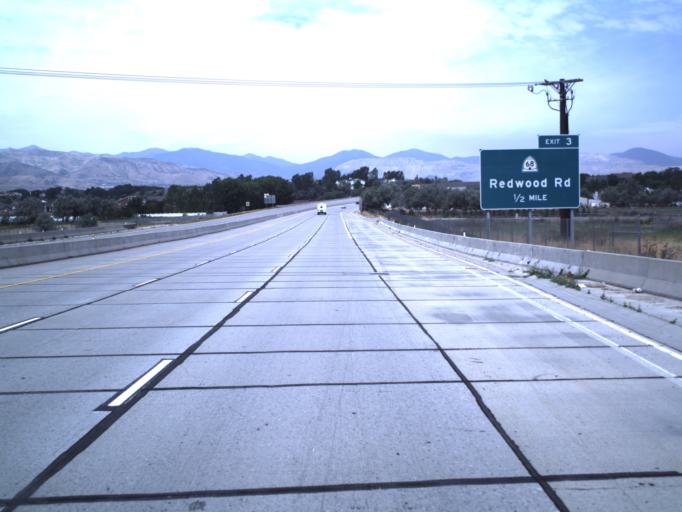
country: US
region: Utah
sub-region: Salt Lake County
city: Bluffdale
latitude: 40.4969
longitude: -111.9214
